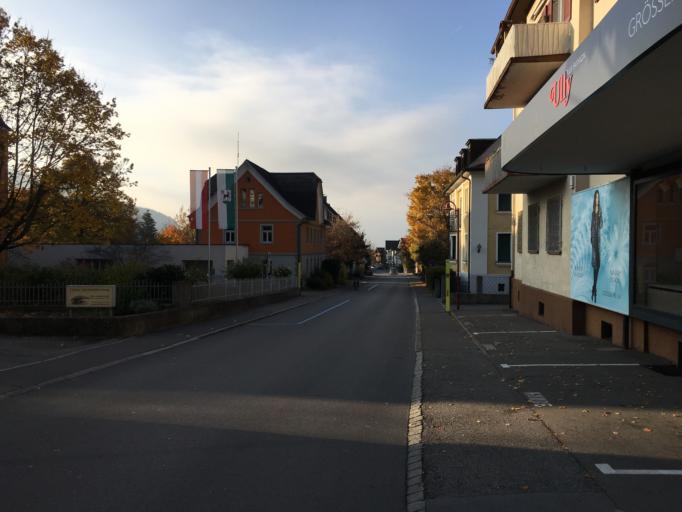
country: AT
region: Vorarlberg
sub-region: Politischer Bezirk Feldkirch
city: Gotzis
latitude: 47.3351
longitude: 9.6445
